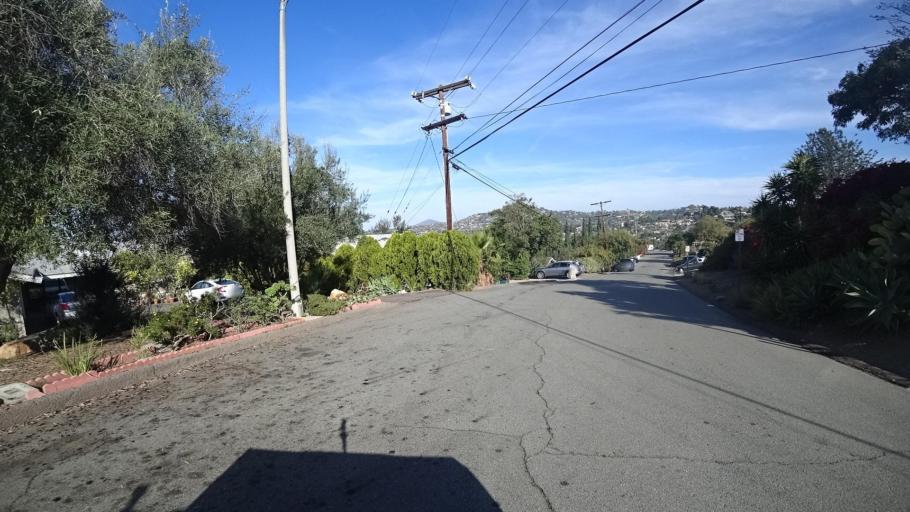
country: US
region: California
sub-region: San Diego County
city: Casa de Oro-Mount Helix
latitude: 32.7381
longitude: -116.9699
